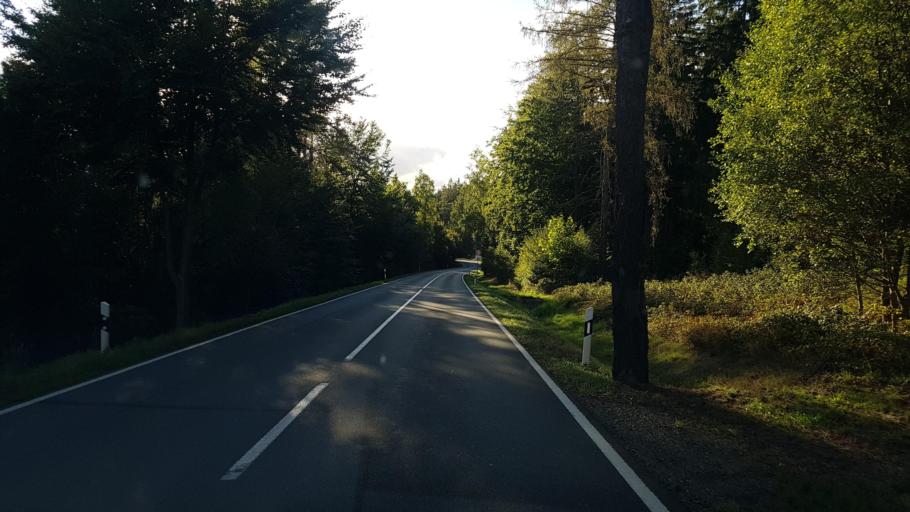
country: DE
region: Thuringia
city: Birkenhugel
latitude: 50.4451
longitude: 11.7215
